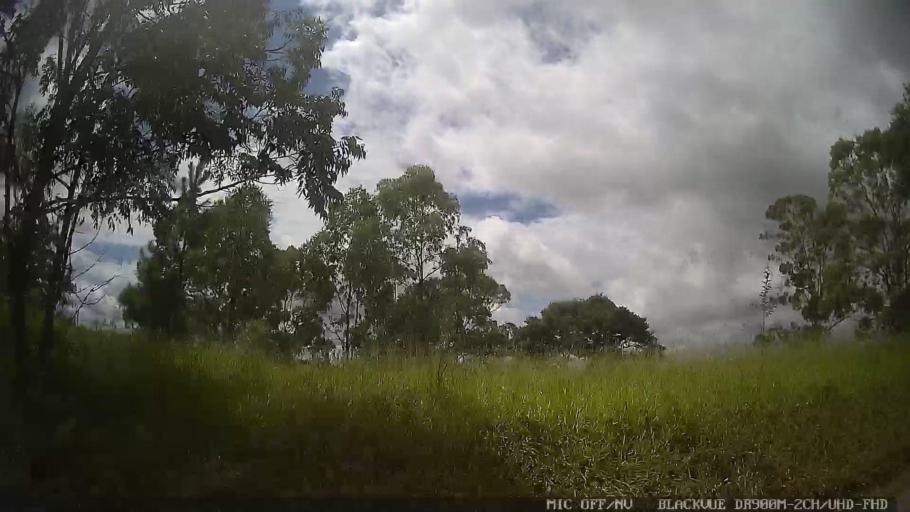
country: BR
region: Sao Paulo
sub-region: Braganca Paulista
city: Braganca Paulista
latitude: -22.8149
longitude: -46.5424
